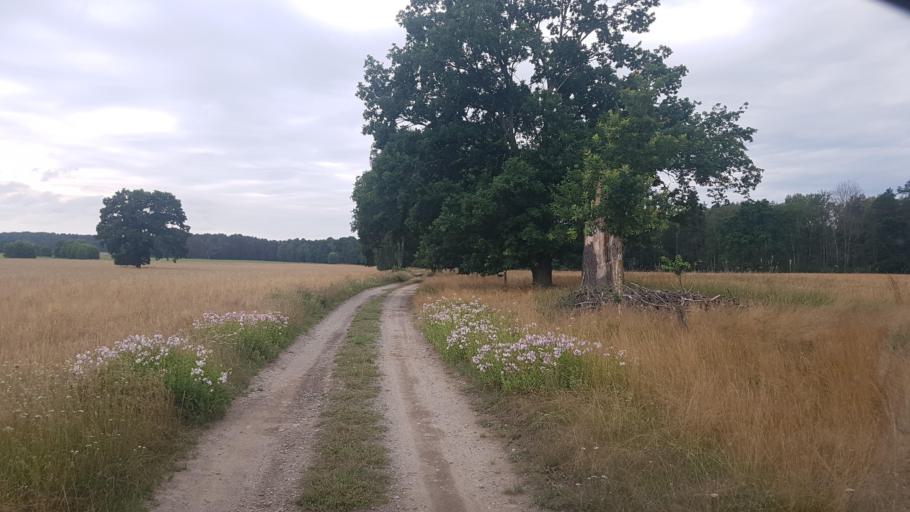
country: DE
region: Brandenburg
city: Crinitz
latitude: 51.7268
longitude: 13.8294
